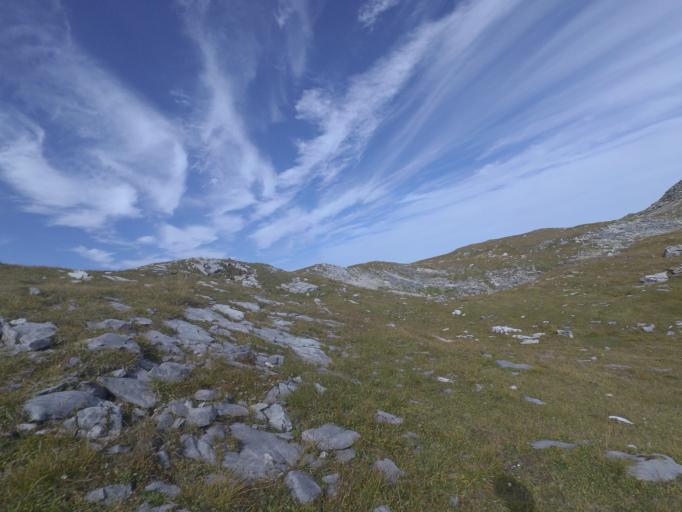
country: AT
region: Salzburg
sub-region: Politischer Bezirk Sankt Johann im Pongau
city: Kleinarl
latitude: 47.2236
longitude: 13.3891
